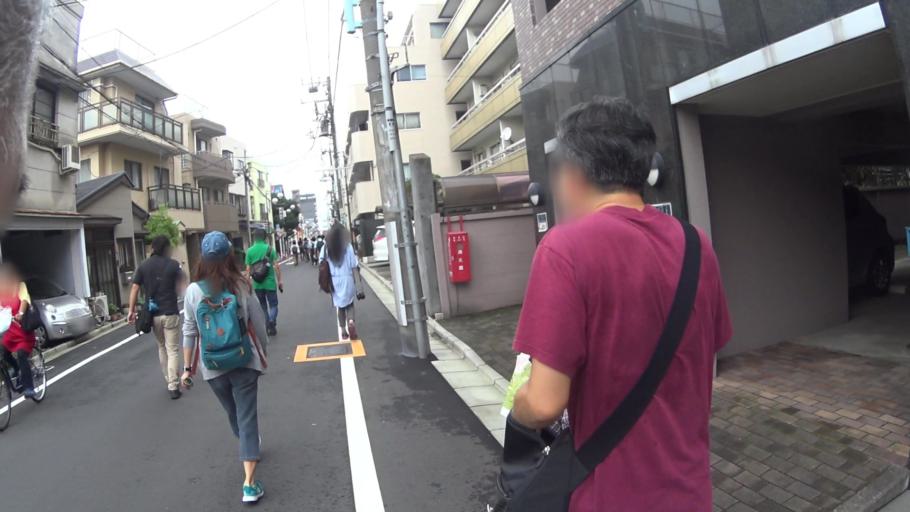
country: JP
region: Tokyo
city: Tokyo
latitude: 35.7384
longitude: 139.6883
